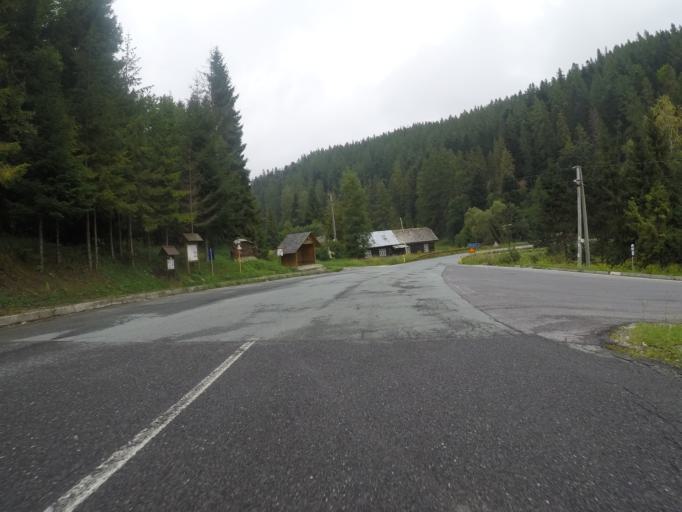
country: SK
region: Kosicky
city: Spisska Nova Ves
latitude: 48.8758
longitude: 20.5221
